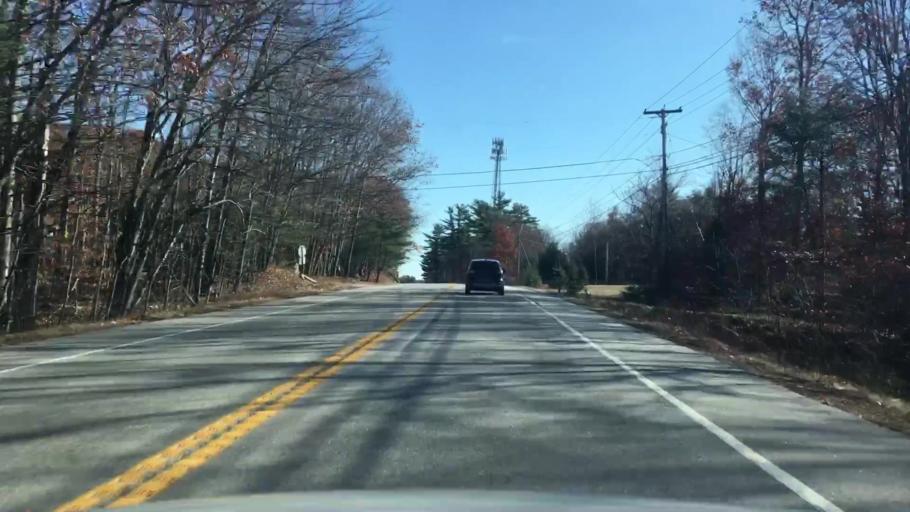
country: US
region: Maine
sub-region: Kennebec County
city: Chelsea
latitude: 44.2802
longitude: -69.6894
